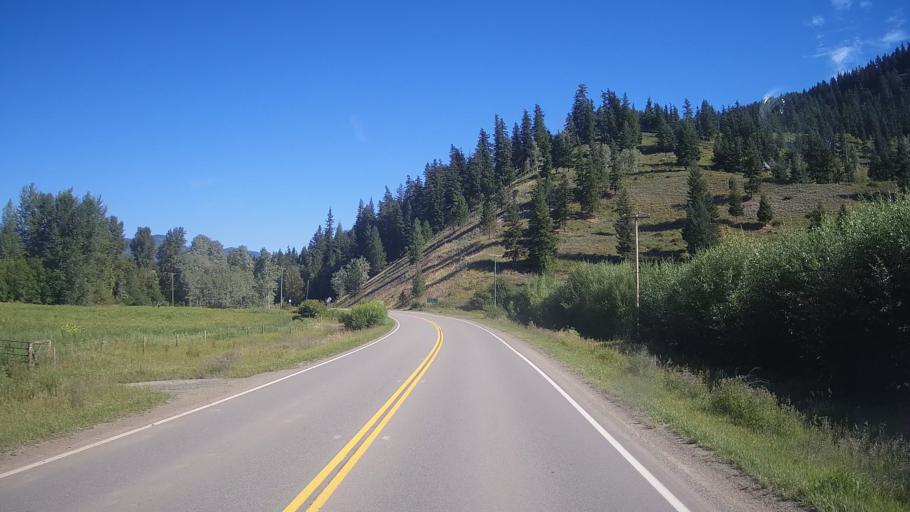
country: CA
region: British Columbia
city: Kamloops
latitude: 51.4347
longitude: -120.2077
